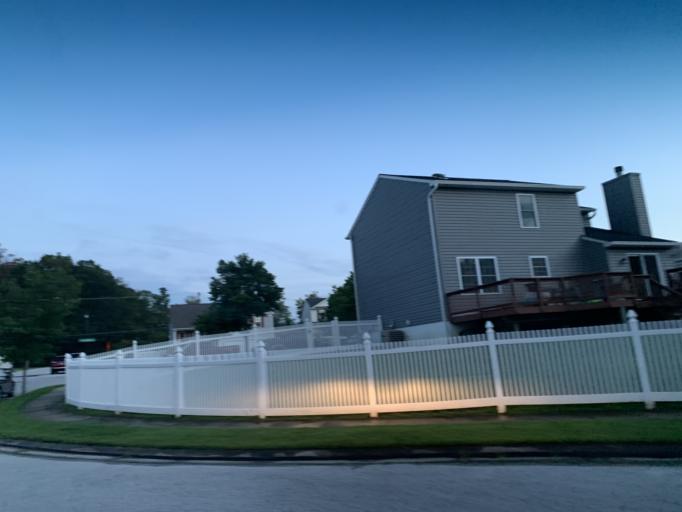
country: US
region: Maryland
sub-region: Baltimore County
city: Middle River
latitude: 39.3536
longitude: -76.4393
